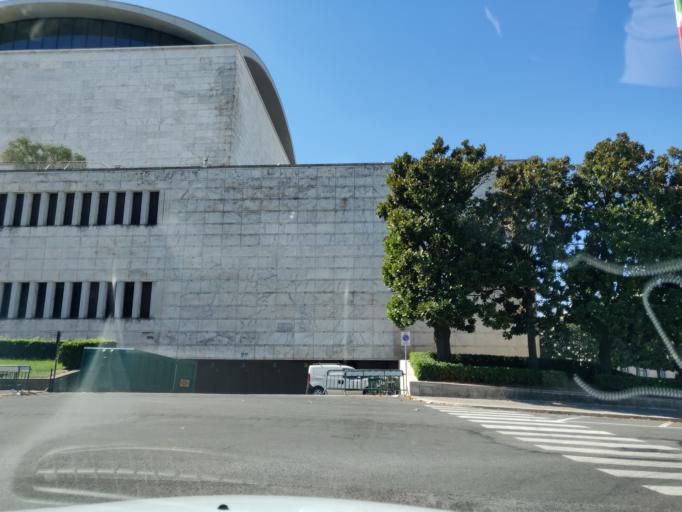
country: IT
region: Latium
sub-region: Citta metropolitana di Roma Capitale
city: Rome
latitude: 41.8348
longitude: 12.4744
